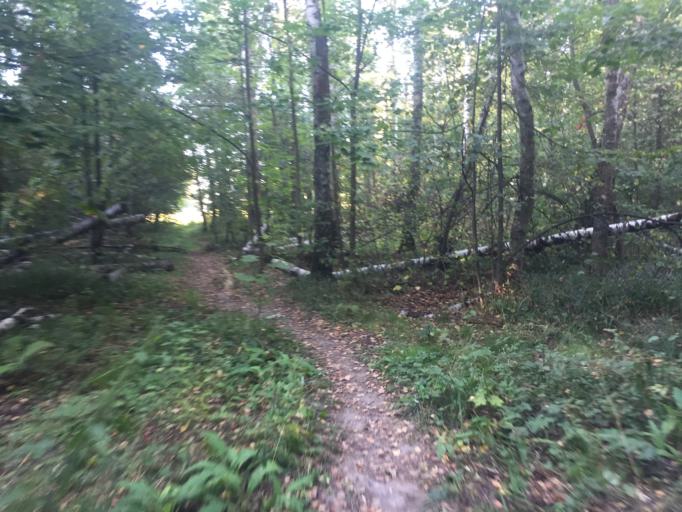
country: RU
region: Moscow
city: Metrogorodok
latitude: 55.8464
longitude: 37.7703
